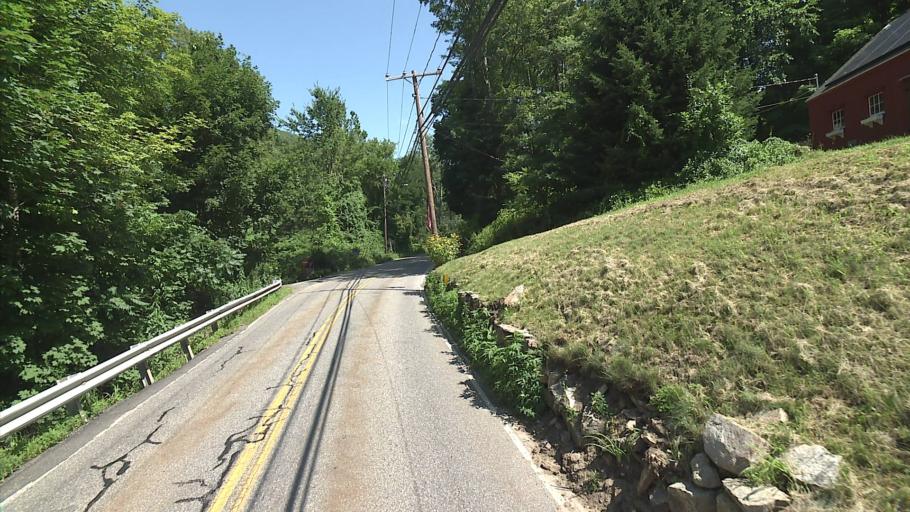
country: US
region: Connecticut
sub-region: Litchfield County
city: New Preston
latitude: 41.6781
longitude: -73.3556
